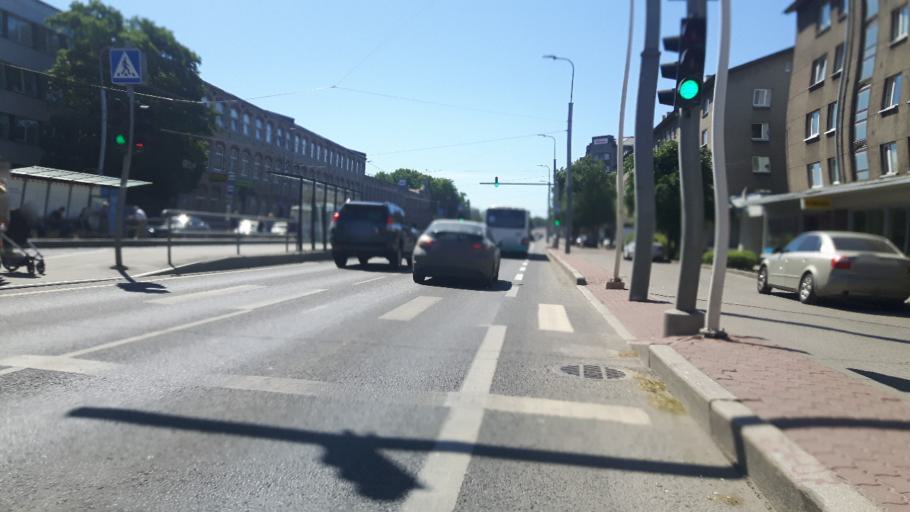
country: EE
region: Harju
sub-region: Tallinna linn
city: Tallinn
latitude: 59.4251
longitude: 24.7424
